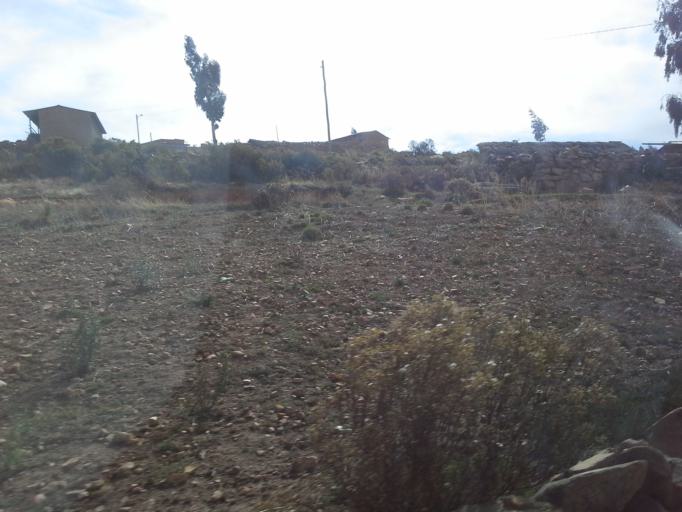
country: BO
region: Cochabamba
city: Colomi
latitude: -17.4386
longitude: -65.8352
